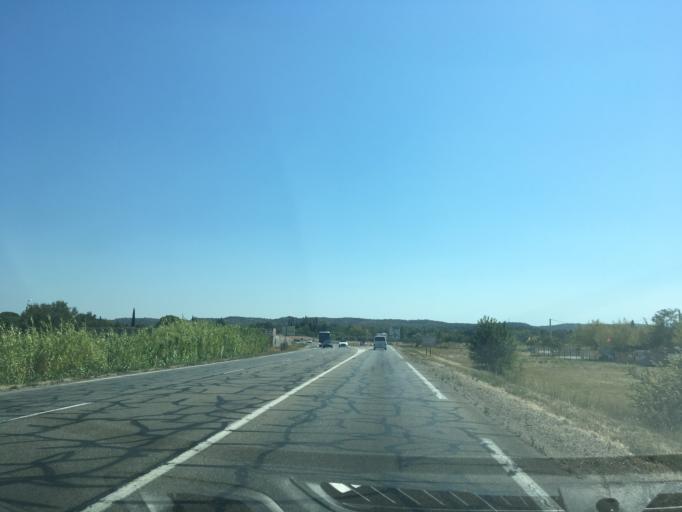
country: FR
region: Provence-Alpes-Cote d'Azur
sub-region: Departement des Bouches-du-Rhone
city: Lancon-Provence
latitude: 43.5972
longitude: 5.1041
